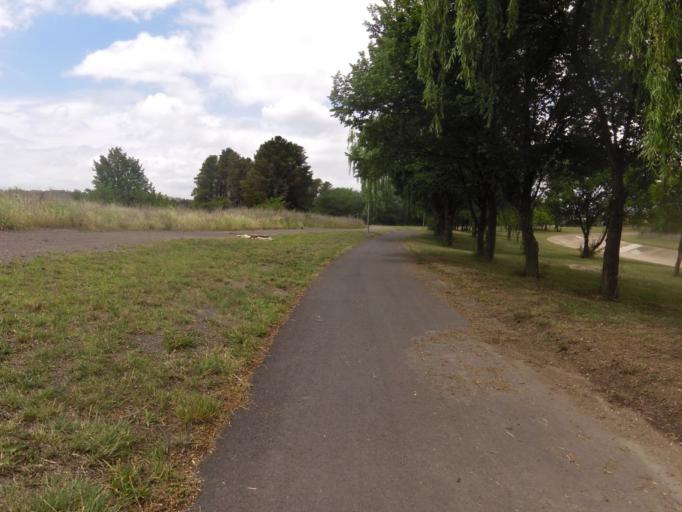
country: AU
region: Australian Capital Territory
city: Macarthur
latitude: -35.4204
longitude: 149.0902
